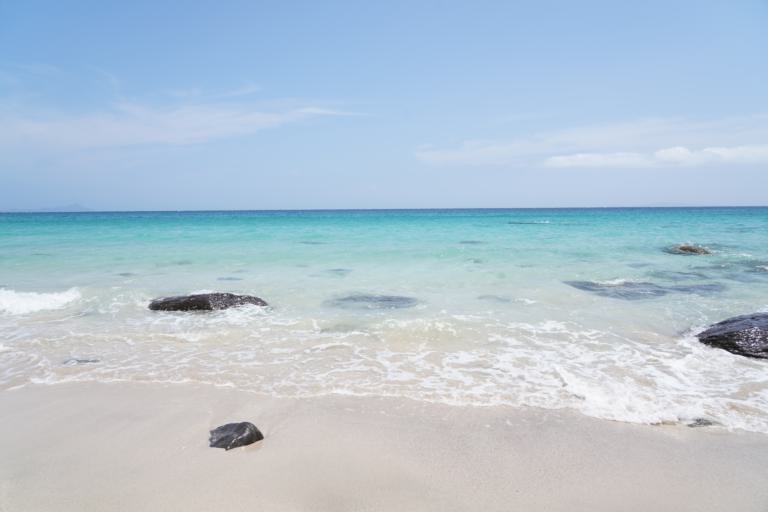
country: JP
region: Nagasaki
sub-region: Hirado Shi
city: Hirado
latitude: 33.1860
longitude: 129.1318
